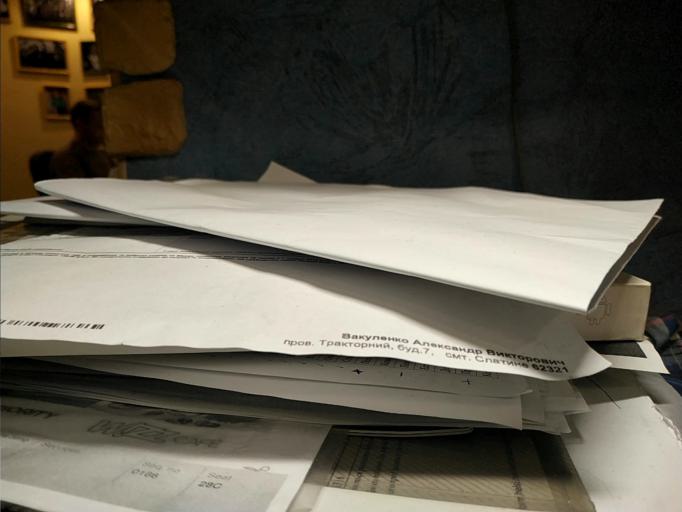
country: RU
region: Tverskaya
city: Zubtsov
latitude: 56.1196
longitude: 34.5769
